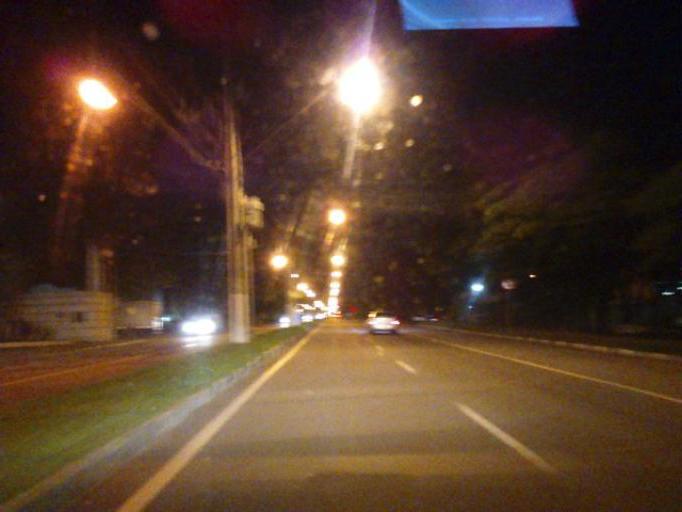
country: BR
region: Sao Paulo
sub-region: Jacarei
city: Jacarei
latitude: -23.2705
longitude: -45.9506
